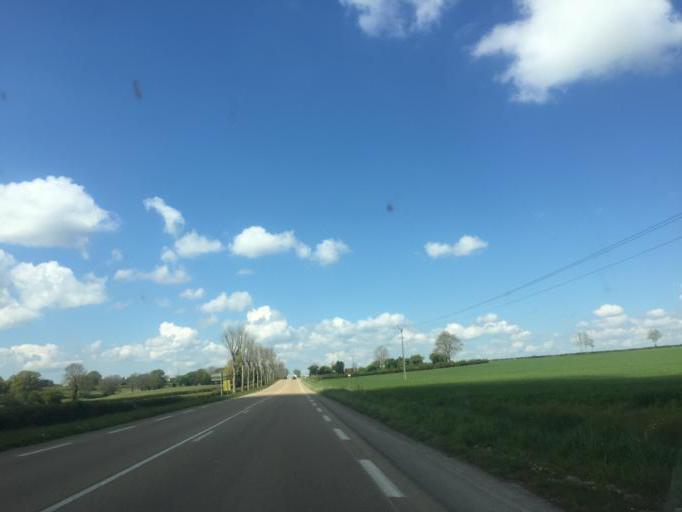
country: FR
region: Bourgogne
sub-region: Departement de l'Yonne
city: Avallon
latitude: 47.4972
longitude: 3.9610
